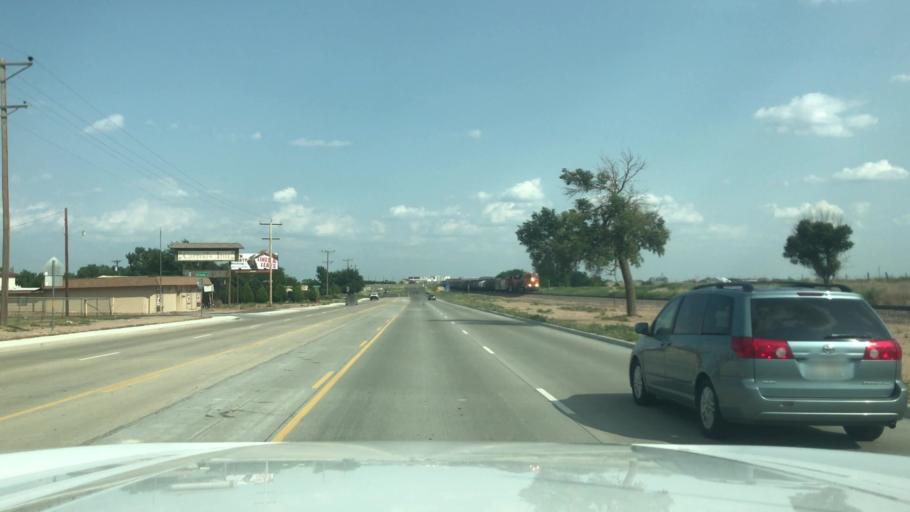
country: US
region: Texas
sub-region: Dallam County
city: Dalhart
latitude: 36.0492
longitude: -102.4981
